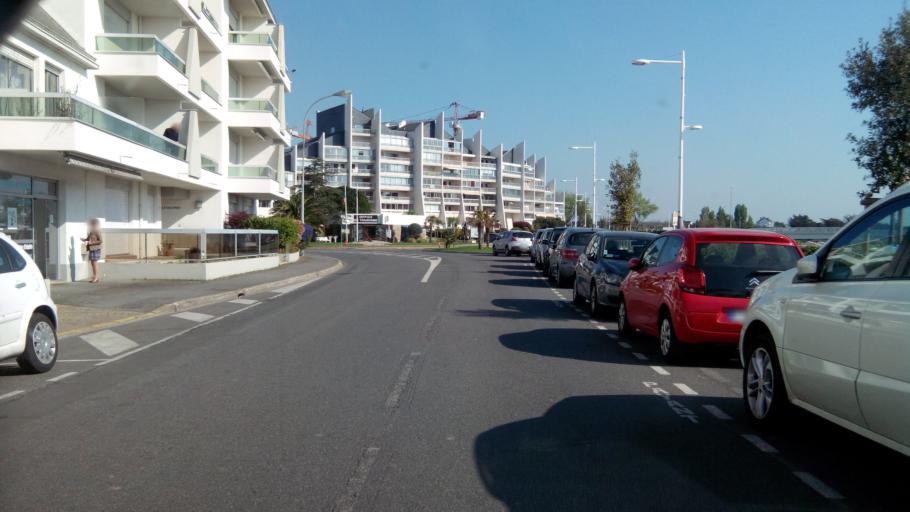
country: FR
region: Pays de la Loire
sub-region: Departement de la Loire-Atlantique
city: Le Pouliguen
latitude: 47.2796
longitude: -2.4281
